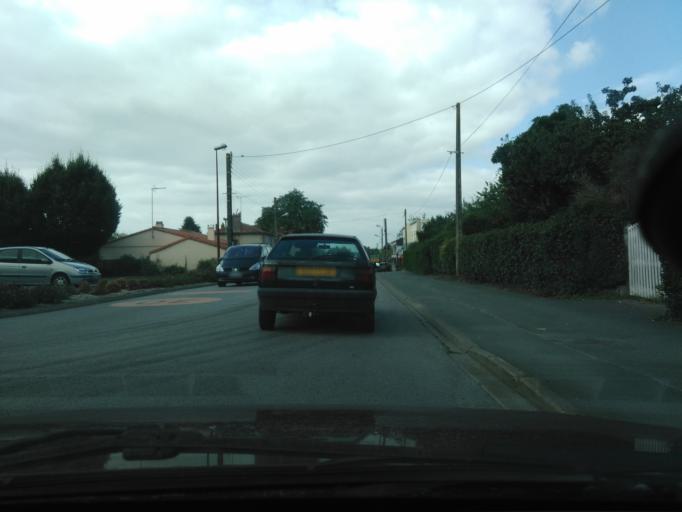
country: FR
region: Pays de la Loire
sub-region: Departement de la Vendee
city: La Ferriere
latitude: 46.7117
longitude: -1.3153
